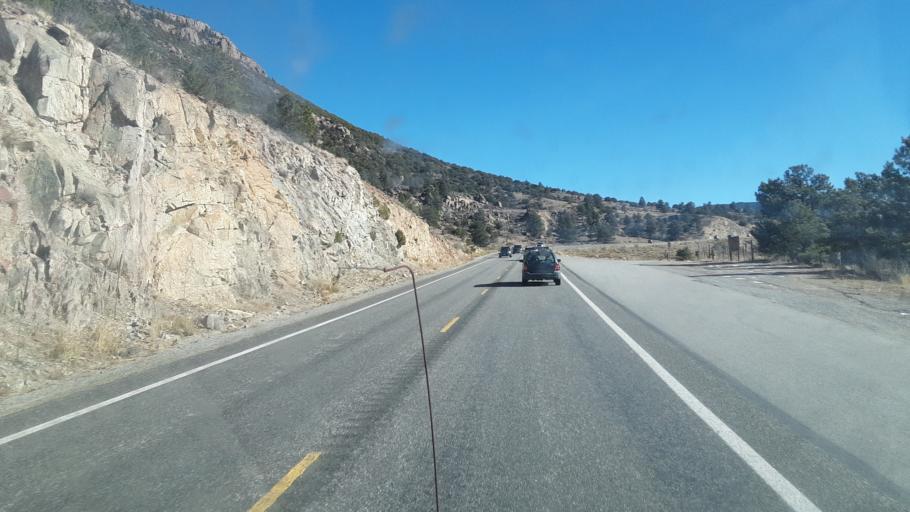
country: US
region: Colorado
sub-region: Chaffee County
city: Buena Vista
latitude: 38.8413
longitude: -106.0116
